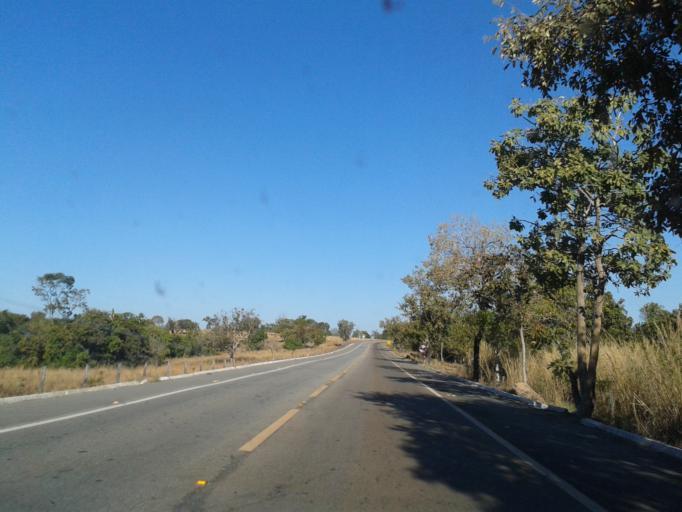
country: BR
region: Goias
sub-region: Mozarlandia
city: Mozarlandia
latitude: -15.2550
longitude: -50.4971
